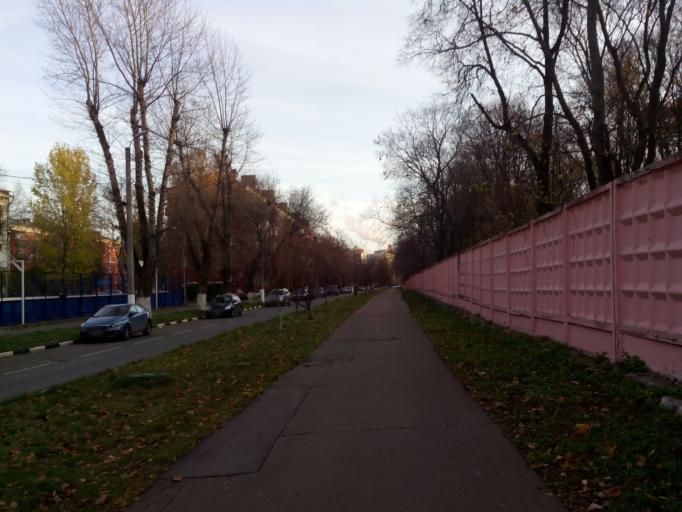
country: RU
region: Moscow
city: Lefortovo
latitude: 55.7715
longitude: 37.7080
